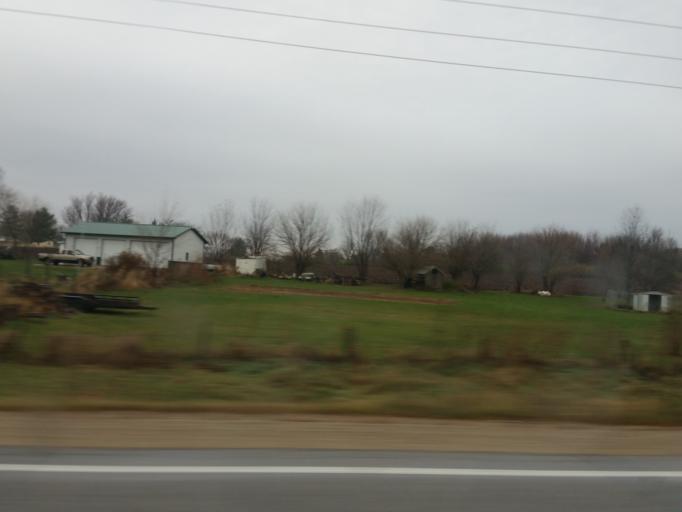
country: US
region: Iowa
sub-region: Black Hawk County
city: Elk Run Heights
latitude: 42.3858
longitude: -92.2466
